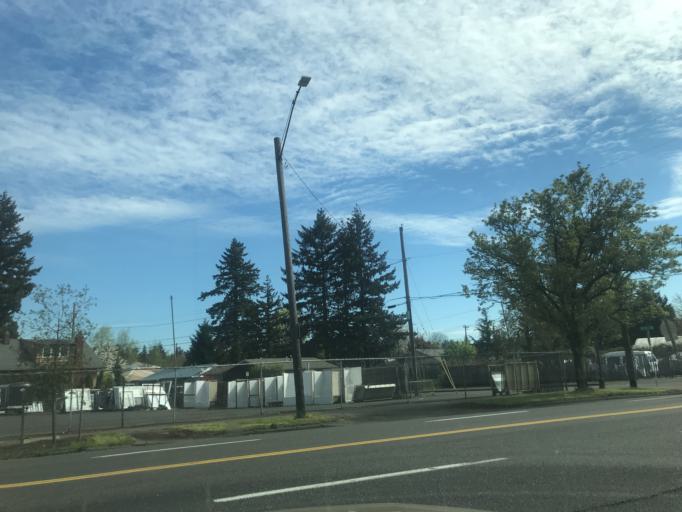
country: US
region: Oregon
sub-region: Multnomah County
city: Lents
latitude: 45.4847
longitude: -122.5841
